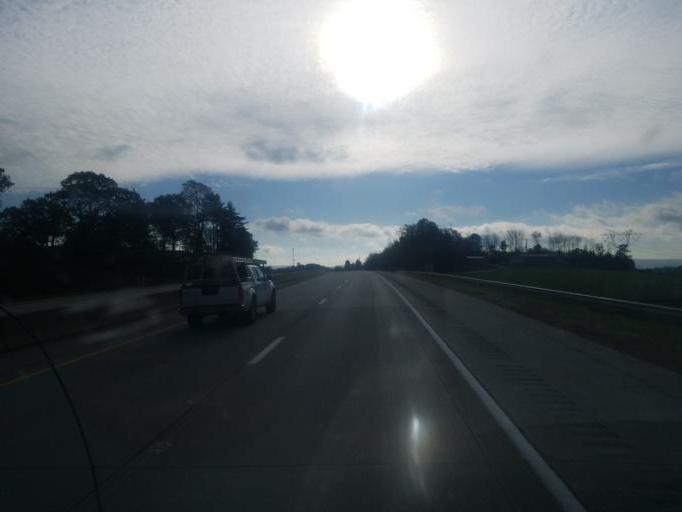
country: US
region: Pennsylvania
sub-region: Indiana County
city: Black Lick
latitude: 40.4496
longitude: -79.1144
